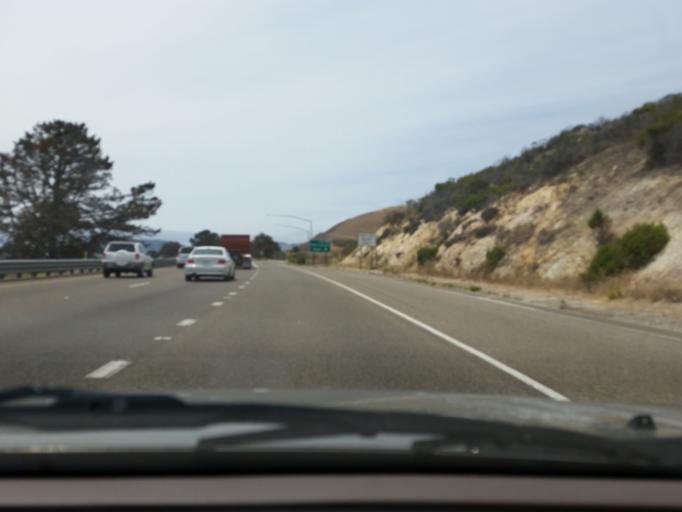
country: US
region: California
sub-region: San Luis Obispo County
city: Pismo Beach
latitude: 35.1497
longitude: -120.6498
